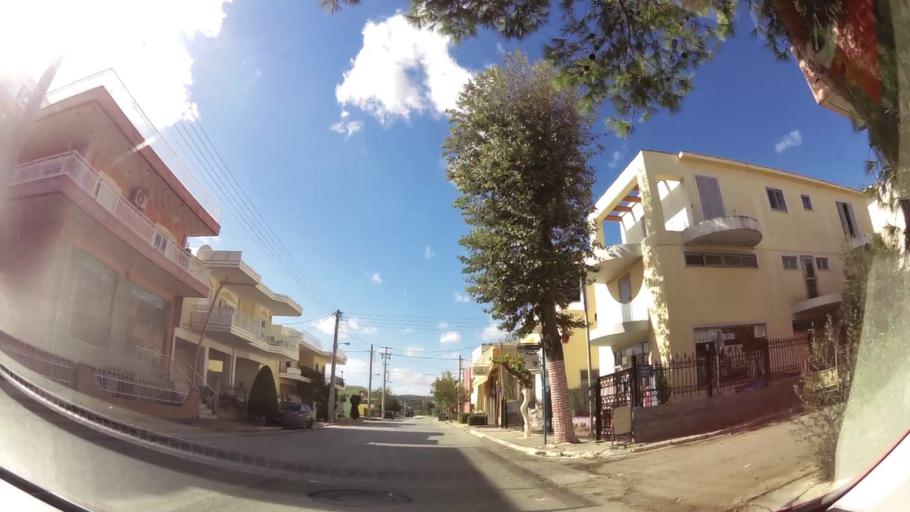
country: GR
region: Attica
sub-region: Nomarchia Anatolikis Attikis
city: Acharnes
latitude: 38.0952
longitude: 23.7330
